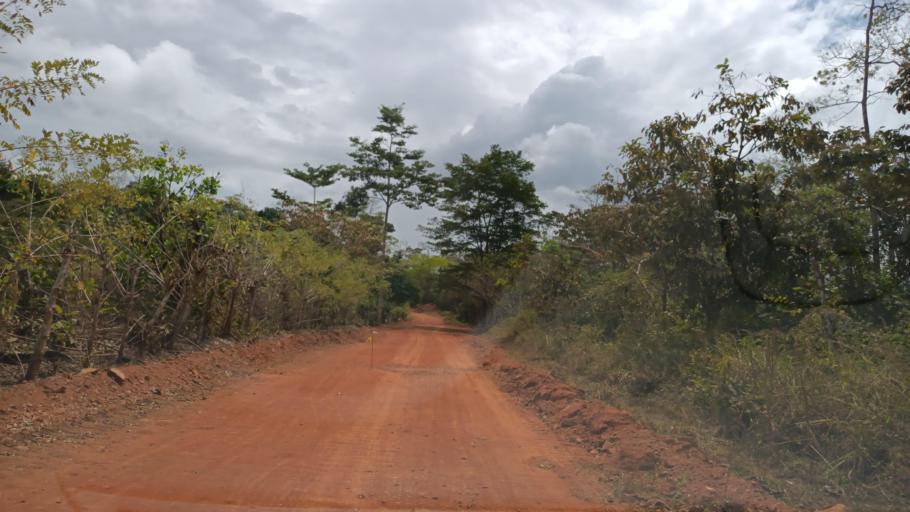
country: PA
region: Panama
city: La Cabima
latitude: 9.1264
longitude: -79.4977
